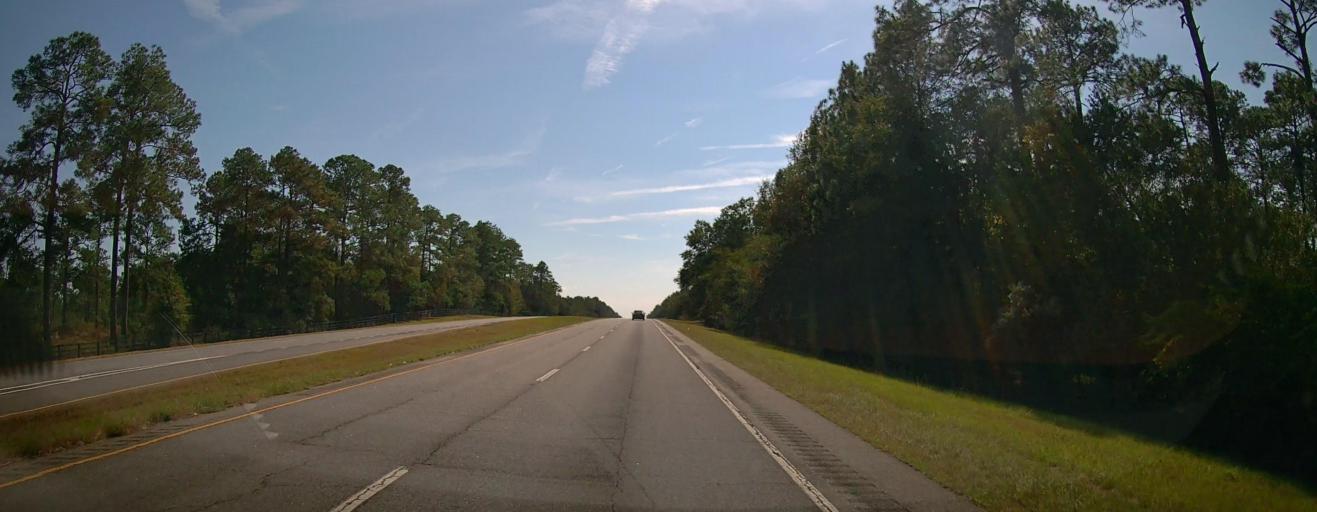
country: US
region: Georgia
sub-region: Lee County
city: Leesburg
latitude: 31.6906
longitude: -83.9931
